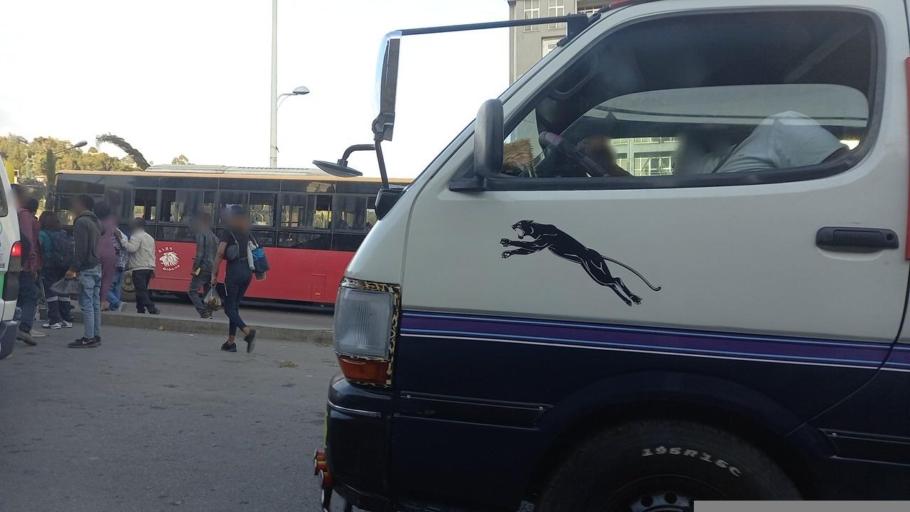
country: ET
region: Adis Abeba
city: Addis Ababa
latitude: 9.0183
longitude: 38.8021
